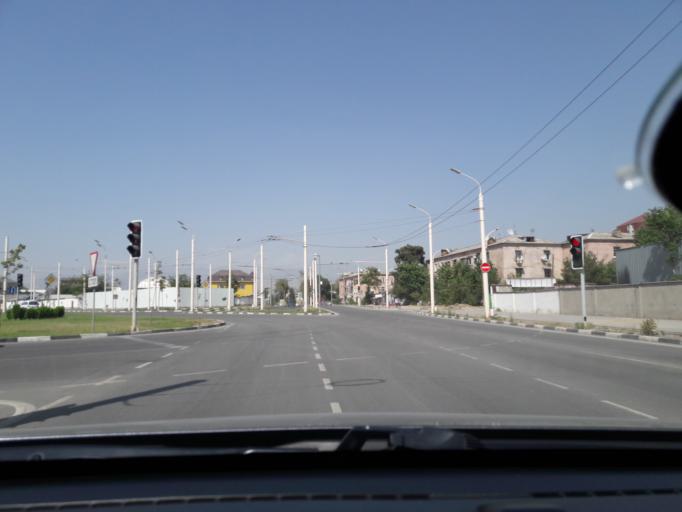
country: TJ
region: Dushanbe
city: Dushanbe
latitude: 38.5363
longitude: 68.7410
